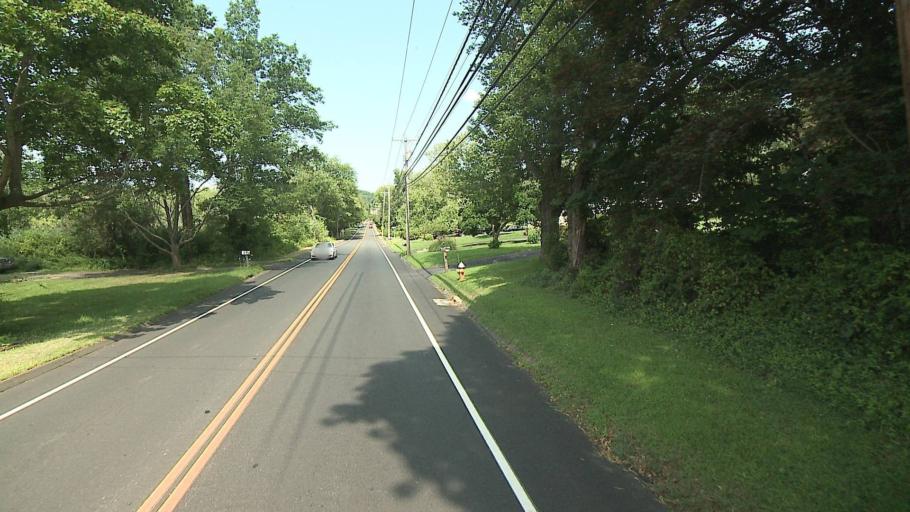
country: US
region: Connecticut
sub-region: Fairfield County
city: Trumbull
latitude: 41.2408
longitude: -73.2712
